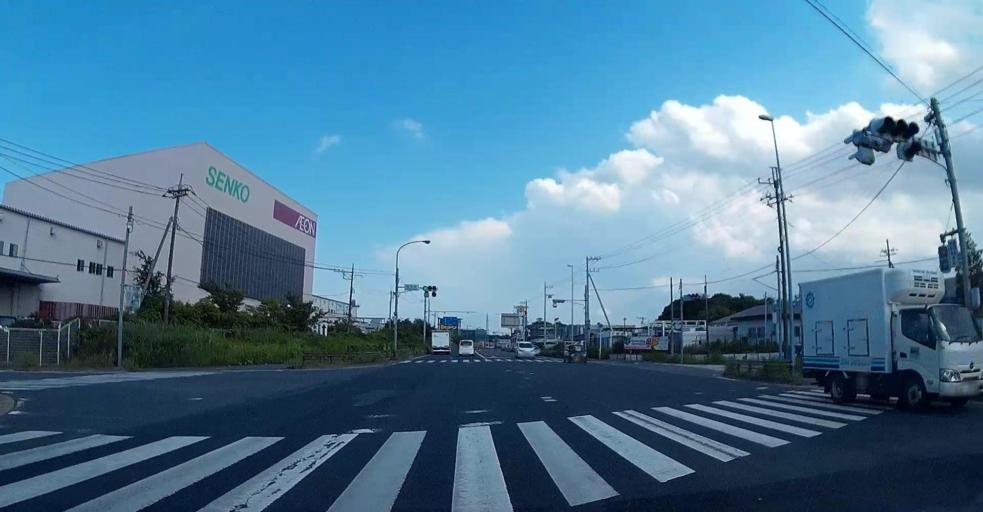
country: JP
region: Chiba
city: Noda
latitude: 35.9831
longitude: 139.8593
